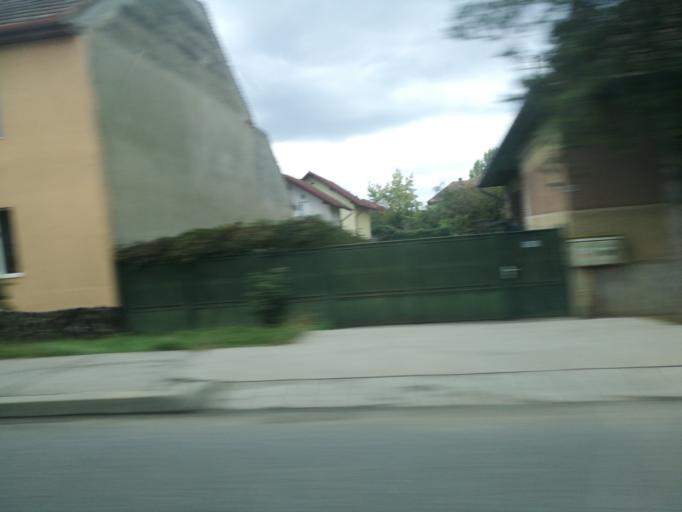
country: RO
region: Mures
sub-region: Comuna Sangeorgiu de Mures
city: Sangeorgiu de Mures
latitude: 46.5705
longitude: 24.5957
